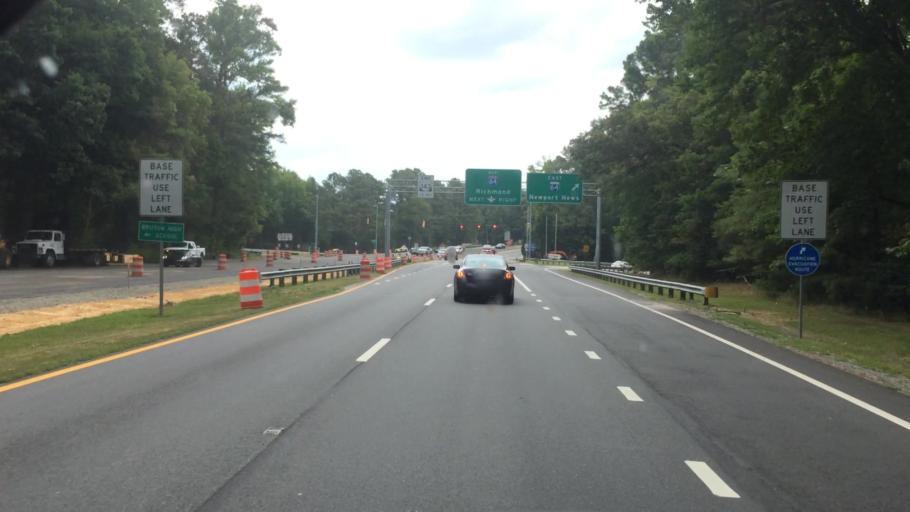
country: US
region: Virginia
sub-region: City of Williamsburg
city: Williamsburg
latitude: 37.3006
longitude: -76.6852
